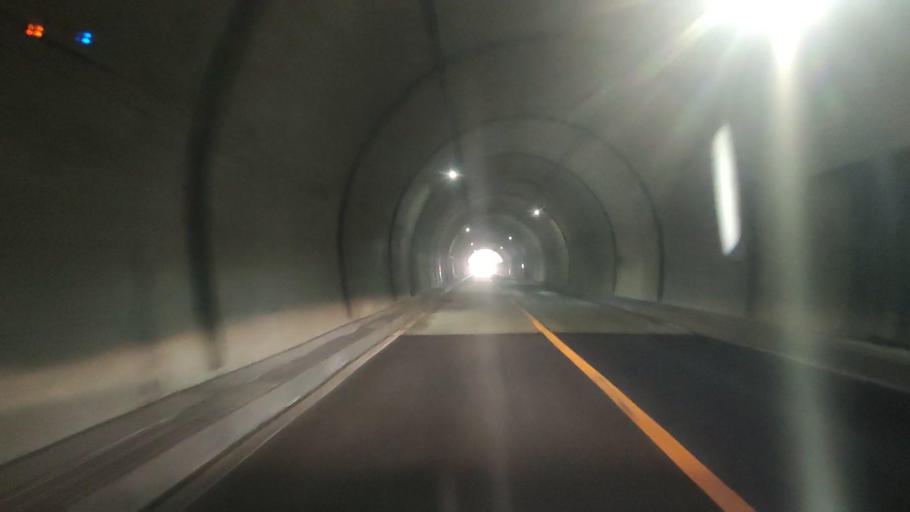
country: JP
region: Oita
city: Saiki
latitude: 32.8840
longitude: 131.9459
